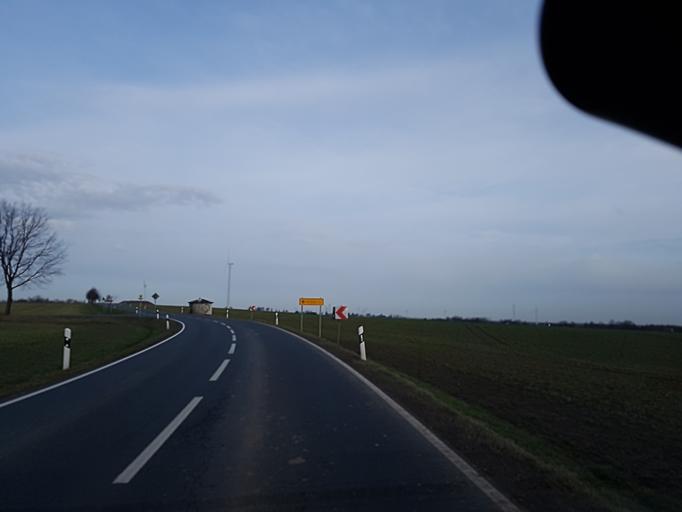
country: DE
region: Saxony
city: Grossweitzschen
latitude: 51.1779
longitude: 13.0265
